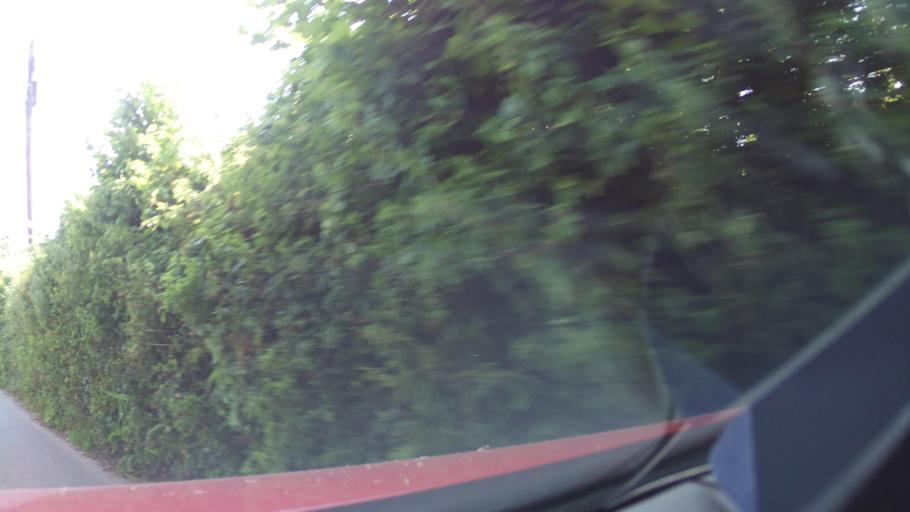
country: GB
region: England
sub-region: Devon
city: Buckfastleigh
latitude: 50.4321
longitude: -3.7492
